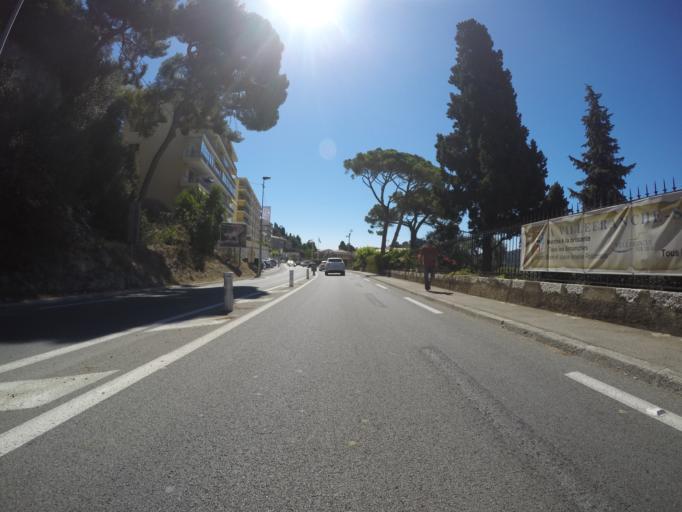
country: FR
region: Provence-Alpes-Cote d'Azur
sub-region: Departement des Alpes-Maritimes
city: Beaulieu-sur-Mer
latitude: 43.7040
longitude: 7.3221
